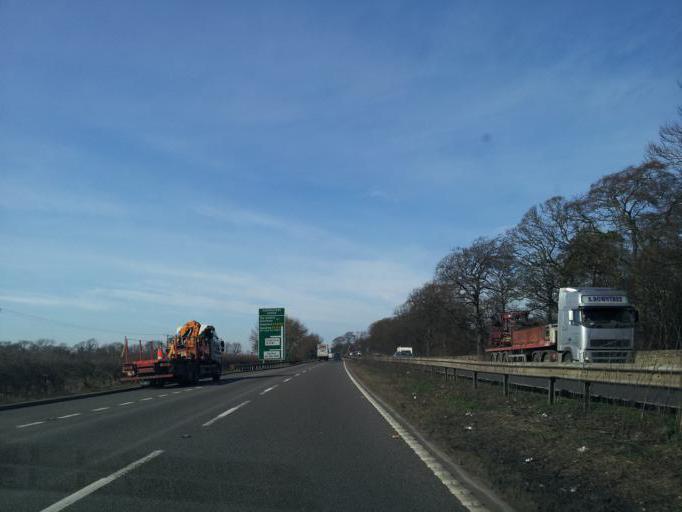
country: GB
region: England
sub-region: Peterborough
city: Wittering
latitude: 52.6239
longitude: -0.4607
